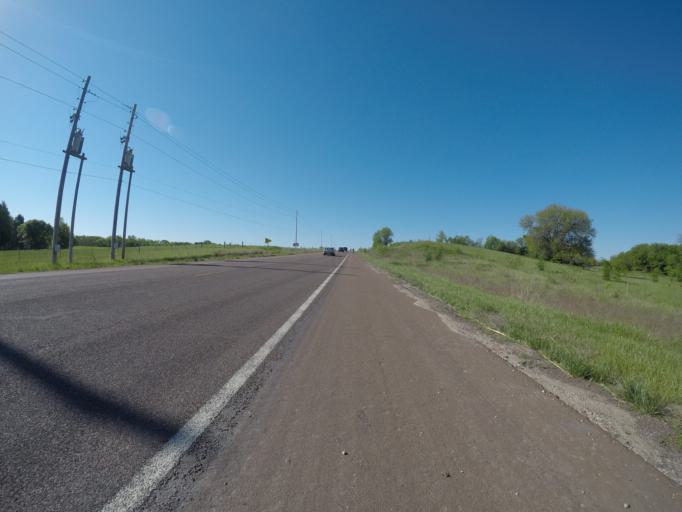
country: US
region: Kansas
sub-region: Douglas County
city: Lawrence
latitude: 39.0339
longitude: -95.3913
